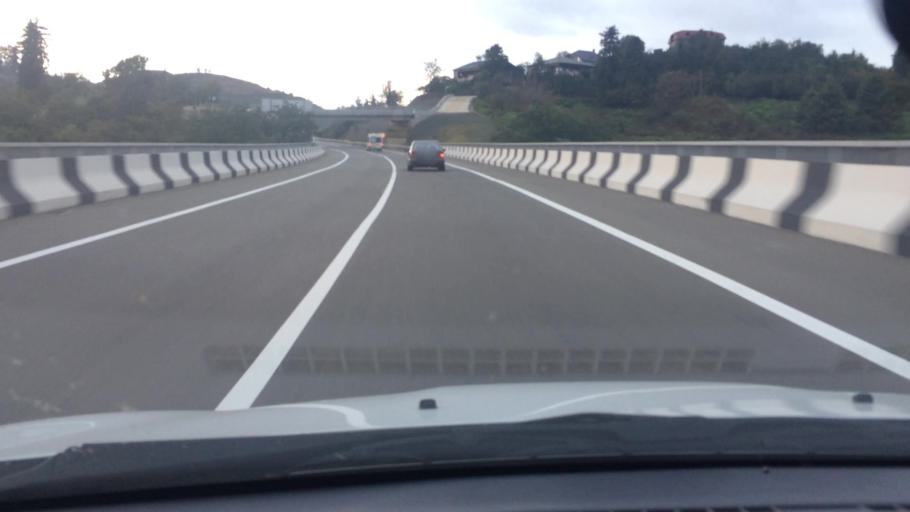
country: GE
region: Ajaria
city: Makhinjauri
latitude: 41.7169
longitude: 41.7518
